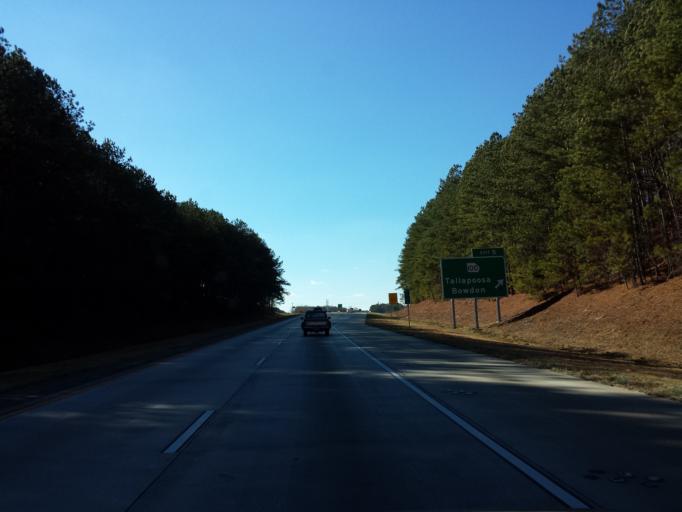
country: US
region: Georgia
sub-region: Haralson County
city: Tallapoosa
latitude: 33.6859
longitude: -85.2564
